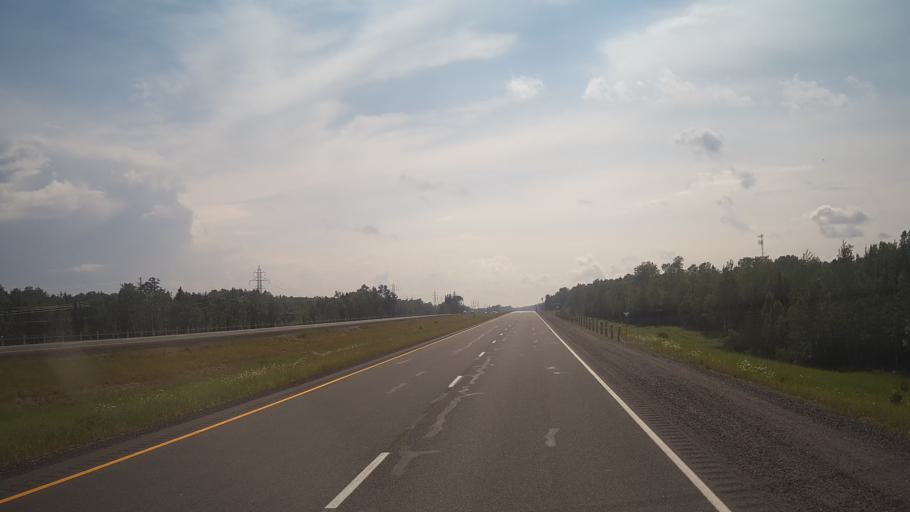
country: CA
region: Ontario
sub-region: Thunder Bay District
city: Thunder Bay
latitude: 48.5434
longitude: -88.9254
